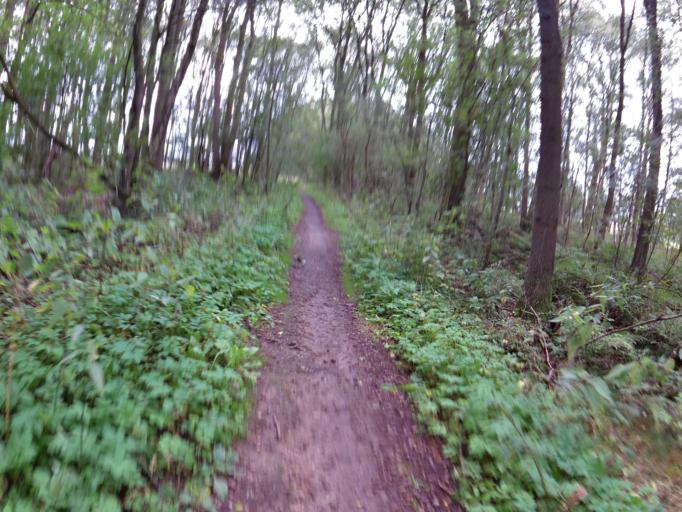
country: NL
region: Gelderland
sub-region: Berkelland
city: Eibergen
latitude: 52.0405
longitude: 6.6885
